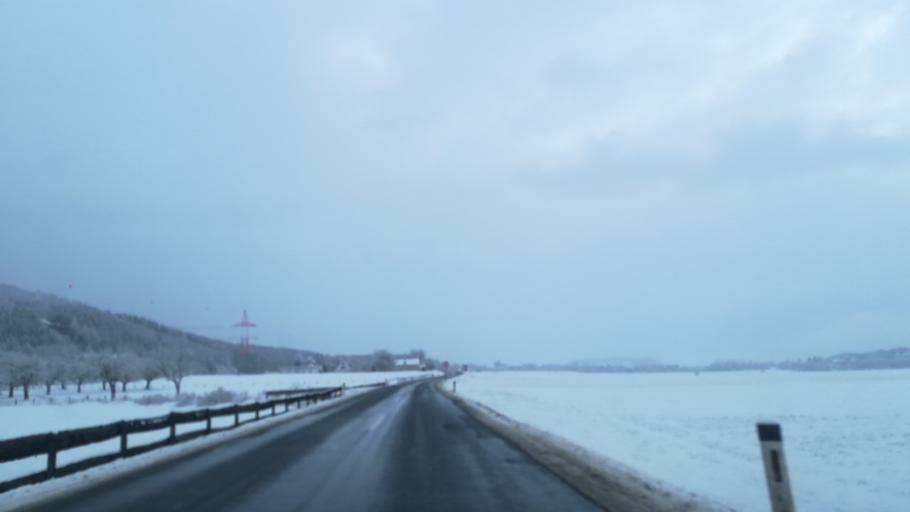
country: AT
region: Styria
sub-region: Politischer Bezirk Murtal
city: Fohnsdorf
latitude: 47.2059
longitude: 14.6416
